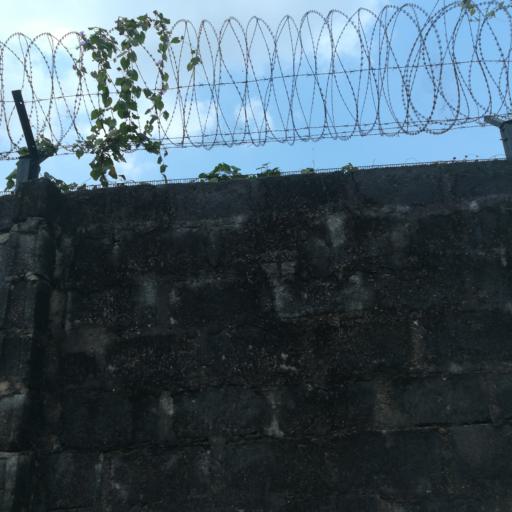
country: NG
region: Rivers
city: Okrika
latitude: 4.8154
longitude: 7.0985
